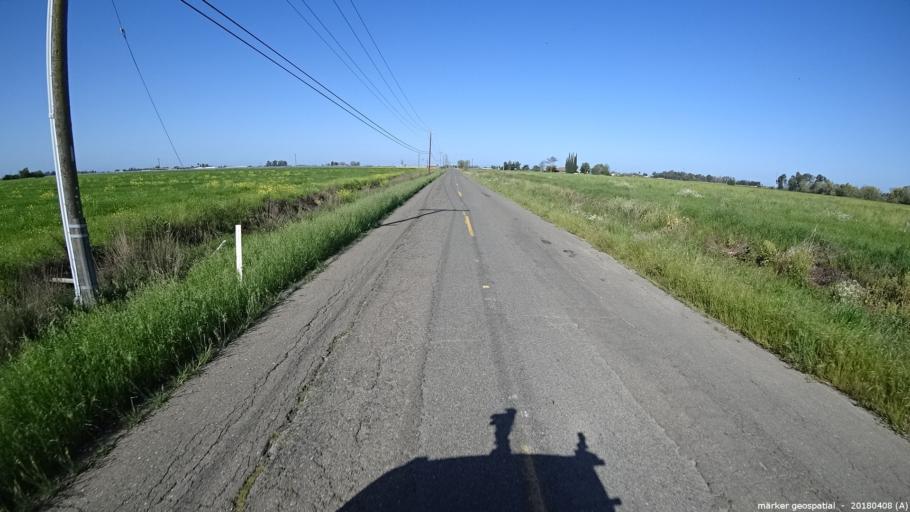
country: US
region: California
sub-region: Sacramento County
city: Elk Grove
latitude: 38.3506
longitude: -121.4042
